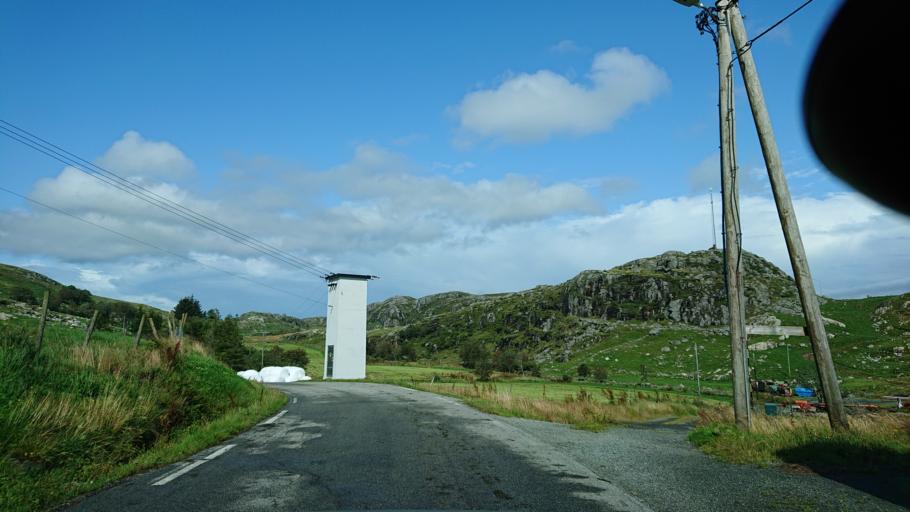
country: NO
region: Rogaland
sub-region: Gjesdal
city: Algard
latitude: 58.6975
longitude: 5.8891
